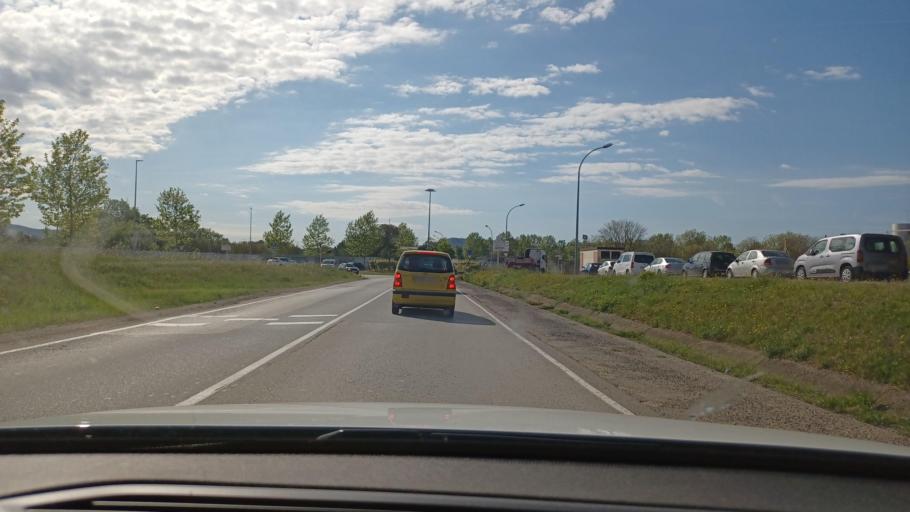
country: ES
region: Catalonia
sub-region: Provincia de Barcelona
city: Vilafranca del Penedes
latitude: 41.3504
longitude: 1.7113
